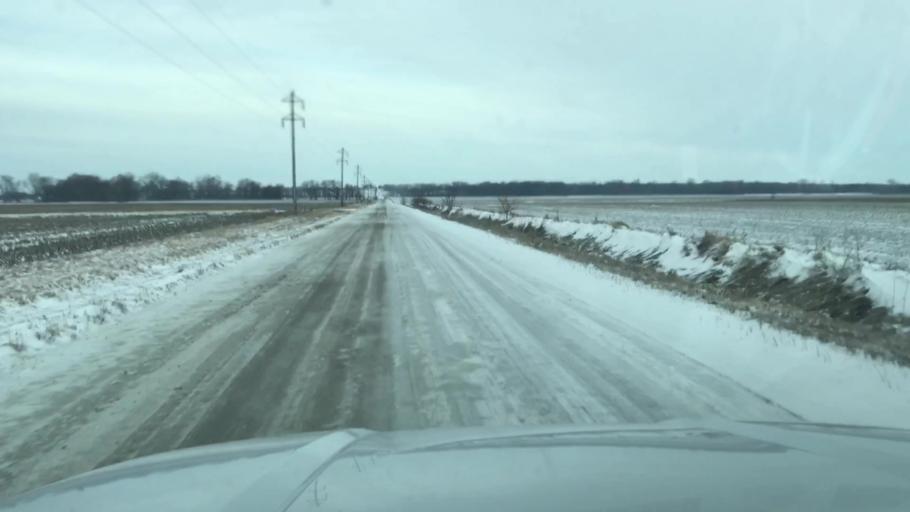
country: US
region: Missouri
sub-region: Holt County
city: Oregon
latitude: 40.1300
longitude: -95.0322
